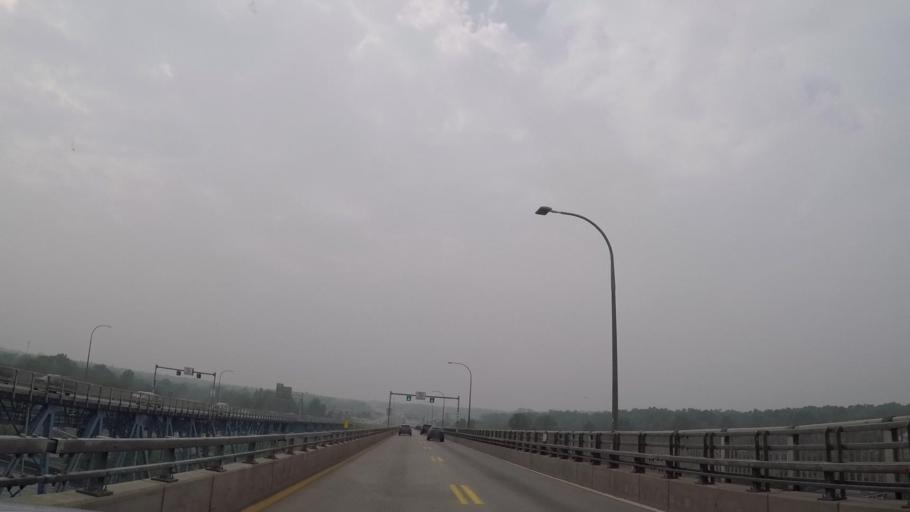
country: US
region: New York
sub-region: Erie County
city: Grandyle Village
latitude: 42.9992
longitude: -78.9377
